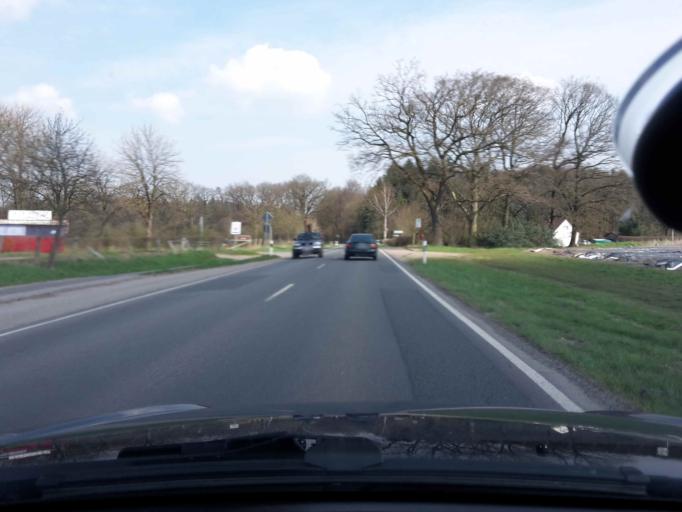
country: DE
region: Lower Saxony
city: Jesteburg
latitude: 53.3217
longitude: 9.9709
